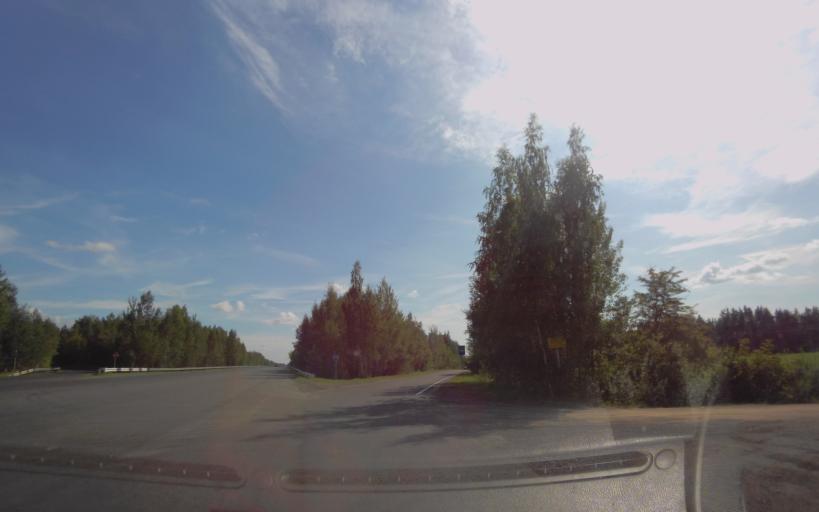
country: BY
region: Minsk
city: Horad Barysaw
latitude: 54.1800
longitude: 28.5710
